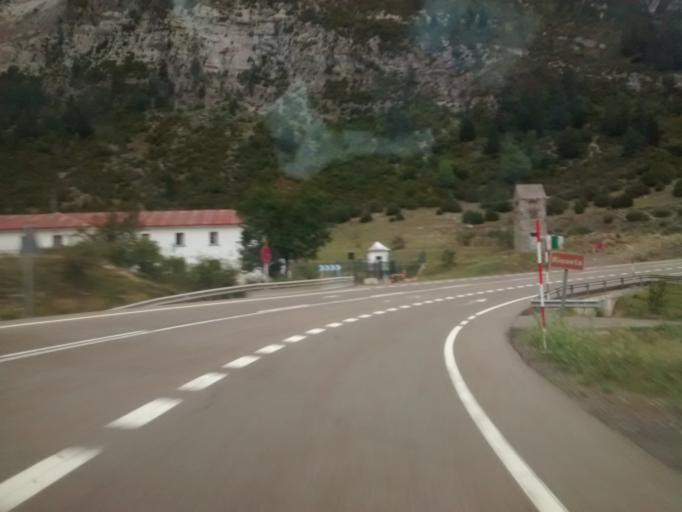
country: ES
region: Aragon
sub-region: Provincia de Huesca
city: Canfranc
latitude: 42.7725
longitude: -0.5185
